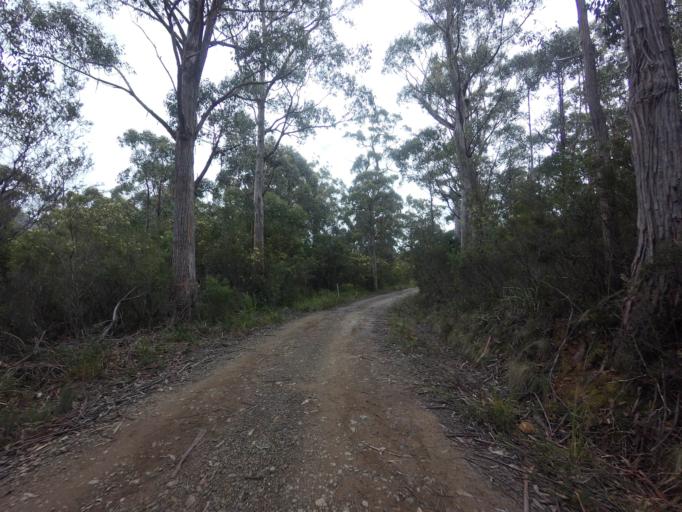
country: AU
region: Tasmania
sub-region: Huon Valley
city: Geeveston
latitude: -43.4583
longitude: 146.9078
